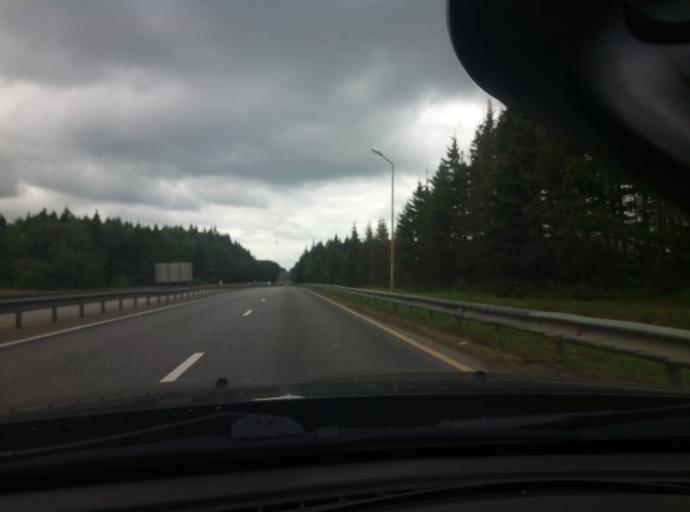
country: RU
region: Kaluga
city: Maloyaroslavets
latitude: 55.0062
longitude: 36.5374
